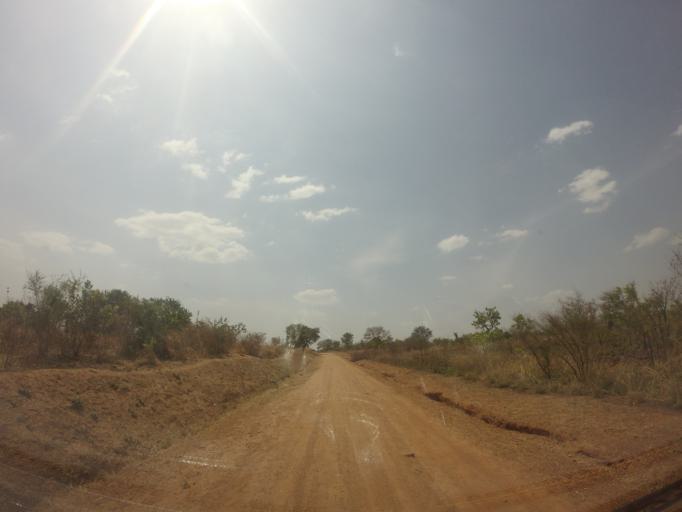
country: UG
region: Northern Region
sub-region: Arua District
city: Arua
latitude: 2.8969
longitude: 31.1292
